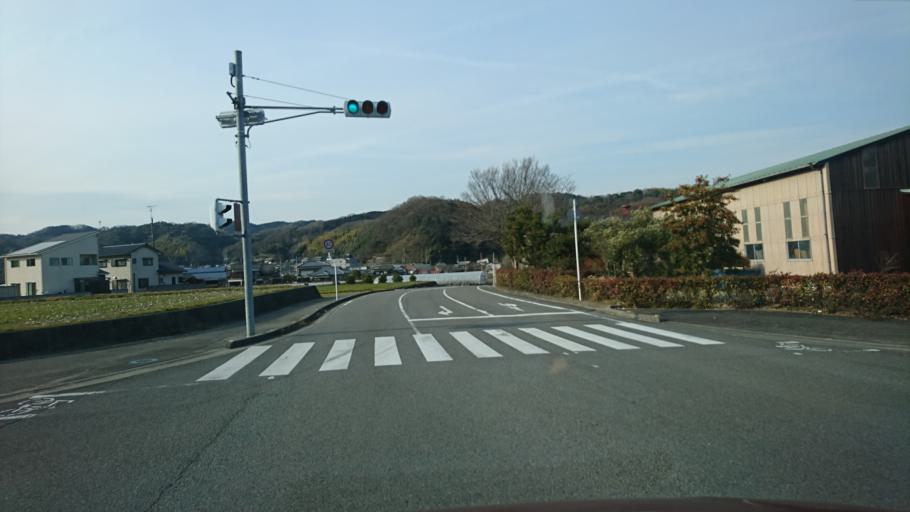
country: JP
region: Ehime
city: Hojo
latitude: 34.0245
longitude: 132.9611
